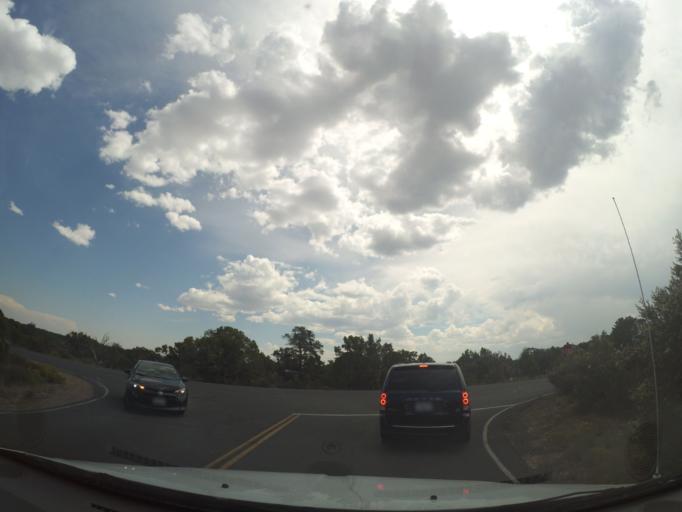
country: US
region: Arizona
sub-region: Coconino County
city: Grand Canyon
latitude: 36.0027
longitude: -111.9236
